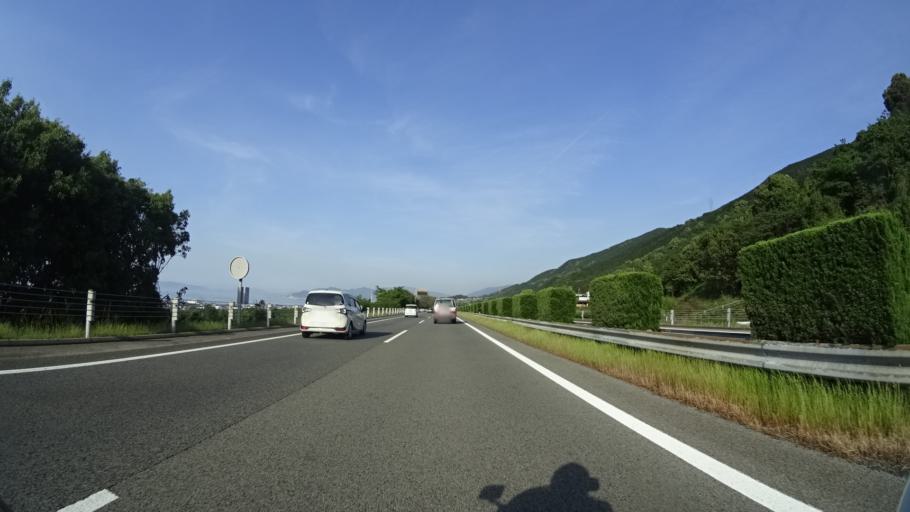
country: JP
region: Ehime
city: Kawanoecho
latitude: 33.9546
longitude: 133.4559
